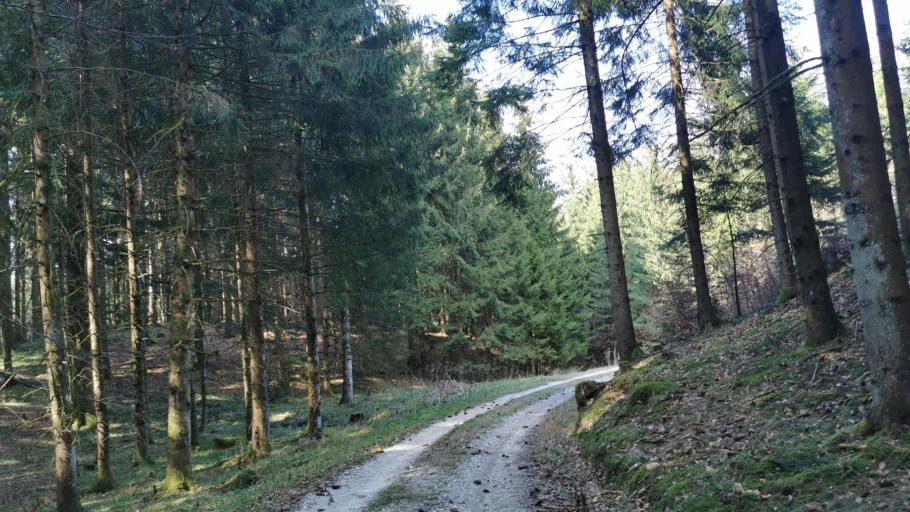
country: AT
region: Salzburg
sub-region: Politischer Bezirk Salzburg-Umgebung
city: Grodig
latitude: 47.7420
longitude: 12.9777
